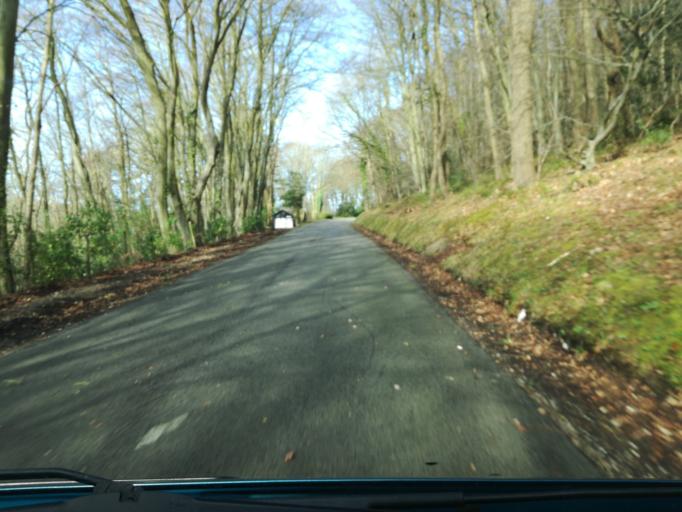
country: FR
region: Haute-Normandie
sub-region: Departement de la Seine-Maritime
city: Yport
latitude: 49.7332
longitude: 0.3231
